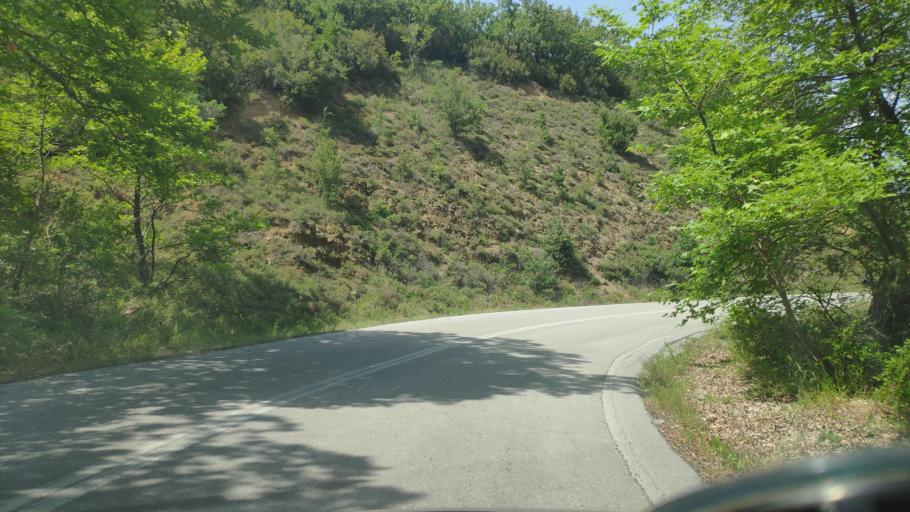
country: GR
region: Epirus
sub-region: Nomos Artas
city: Ano Kalentini
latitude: 39.2488
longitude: 21.1905
